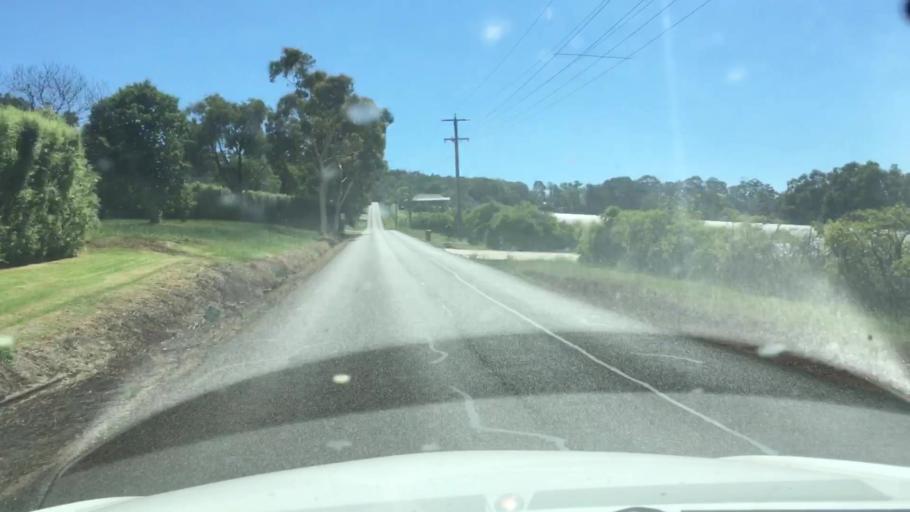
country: AU
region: Victoria
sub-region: Yarra Ranges
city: Mount Evelyn
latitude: -37.8194
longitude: 145.4188
